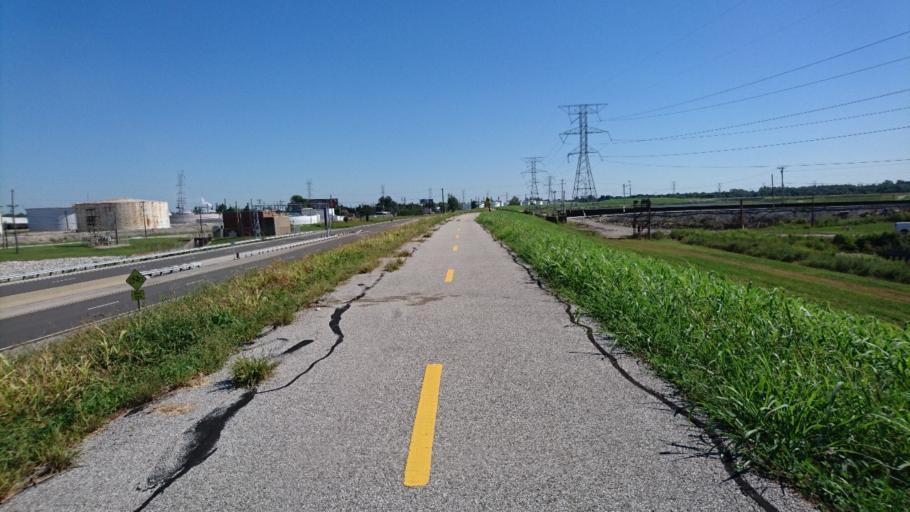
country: US
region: Illinois
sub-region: Madison County
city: Wood River
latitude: 38.8537
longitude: -90.1050
